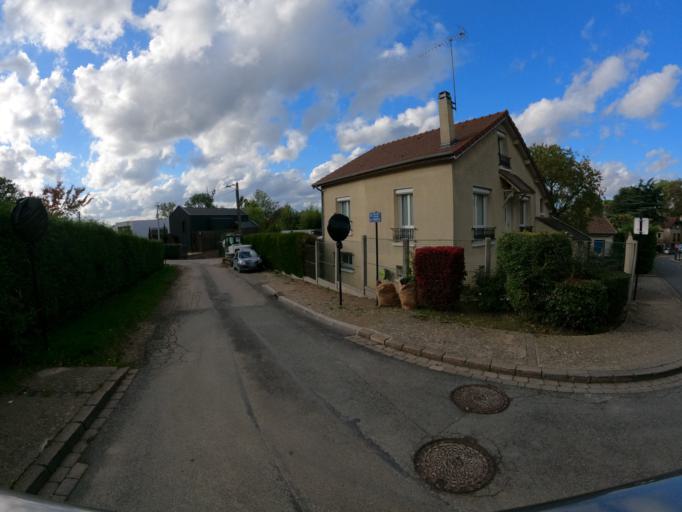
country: FR
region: Ile-de-France
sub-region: Departement de Seine-et-Marne
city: Chessy
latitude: 48.8825
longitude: 2.7638
